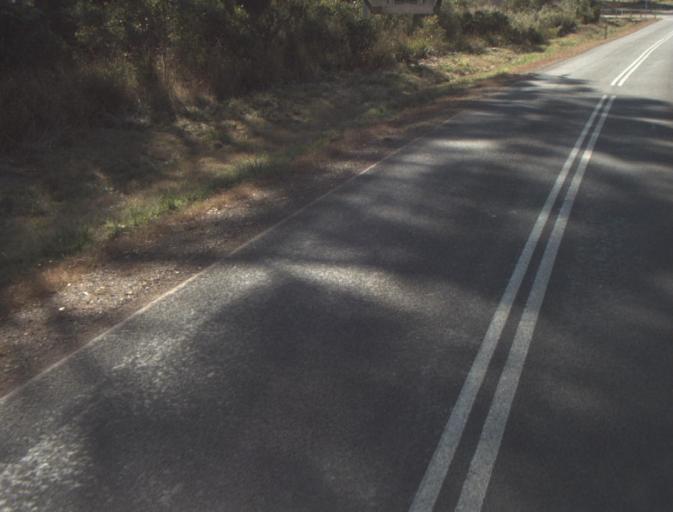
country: AU
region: Tasmania
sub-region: Launceston
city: Mayfield
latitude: -41.2830
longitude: 147.1260
